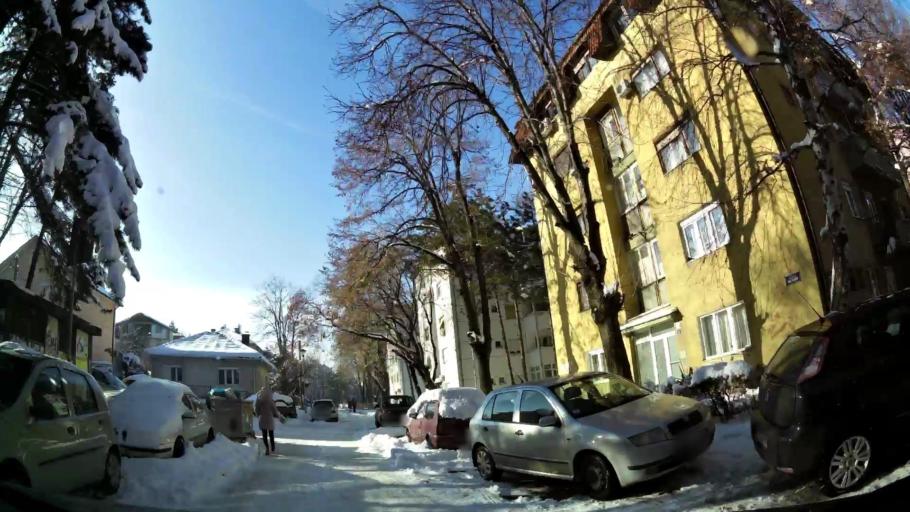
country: RS
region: Central Serbia
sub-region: Belgrade
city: Palilula
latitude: 44.8120
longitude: 20.5182
